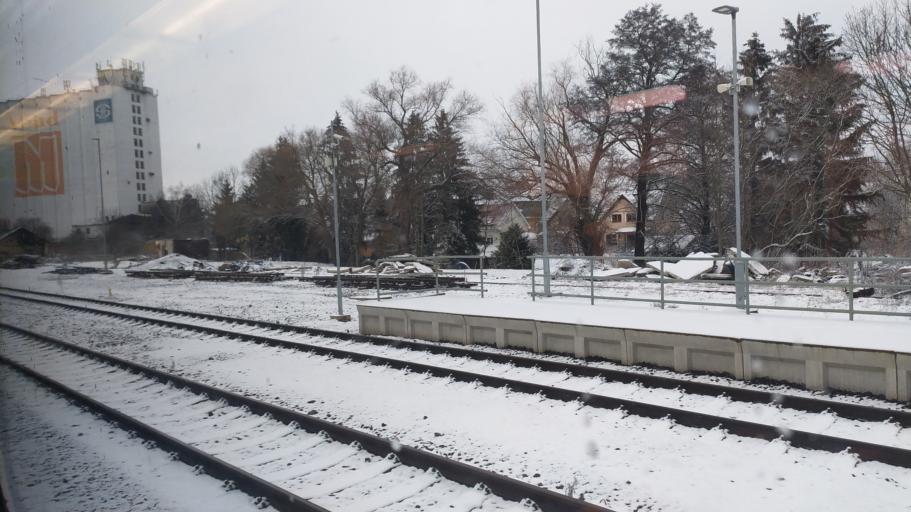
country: CZ
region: Central Bohemia
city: Trebotov
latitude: 50.0322
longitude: 14.3089
